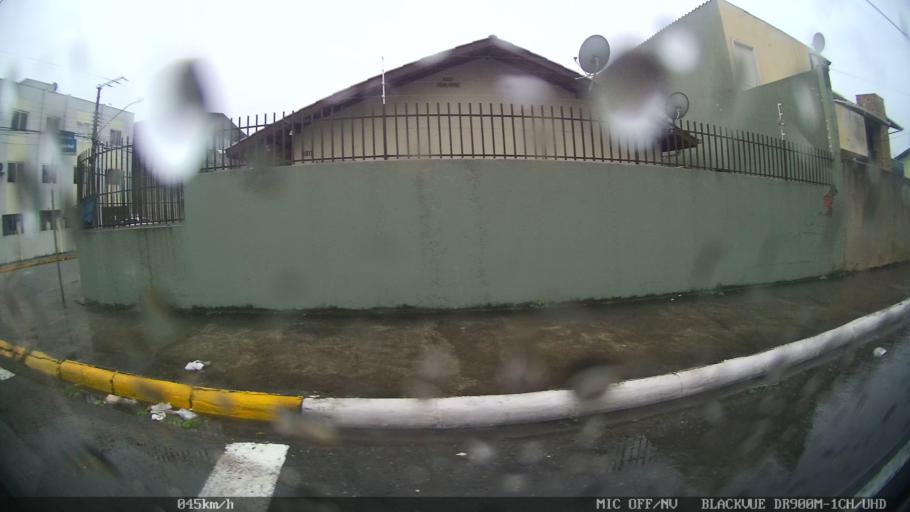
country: BR
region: Santa Catarina
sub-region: Itajai
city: Itajai
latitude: -26.9187
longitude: -48.6800
